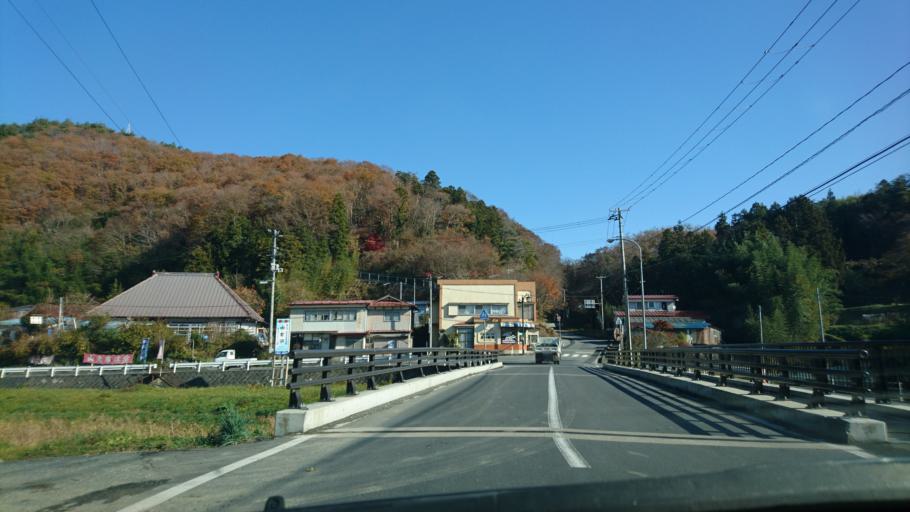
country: JP
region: Iwate
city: Ichinoseki
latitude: 38.9993
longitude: 141.2574
